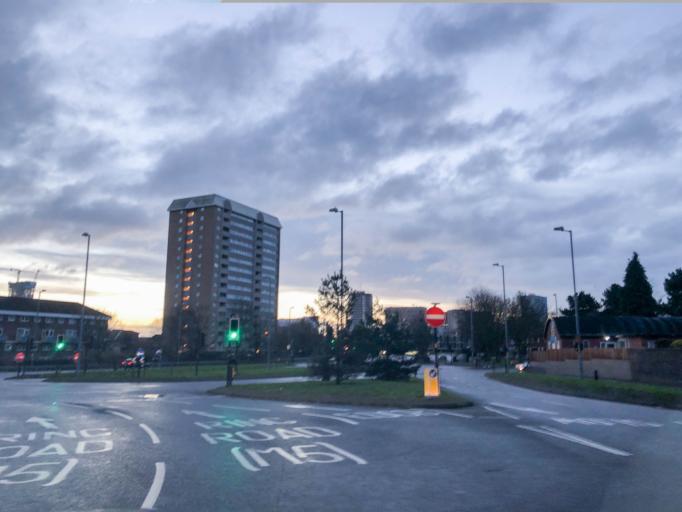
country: GB
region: England
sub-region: City and Borough of Birmingham
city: Hockley
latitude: 52.4780
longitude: -1.9275
